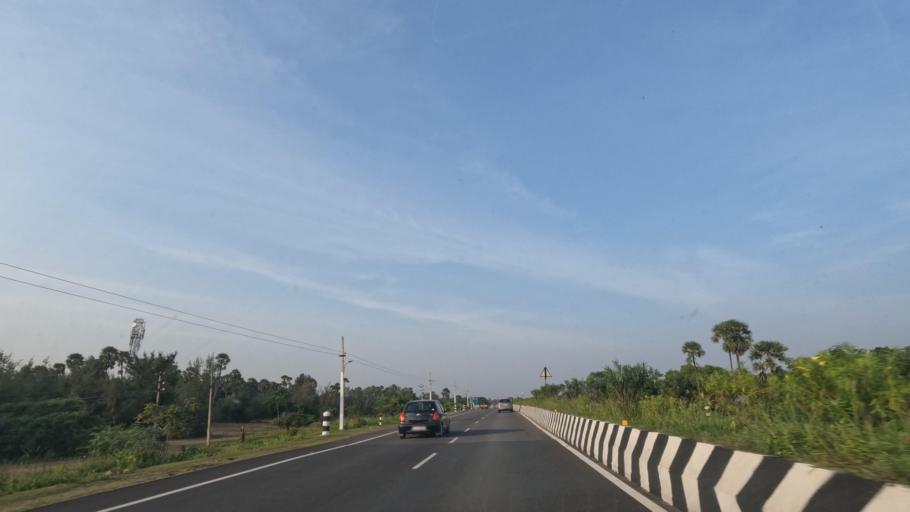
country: IN
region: Tamil Nadu
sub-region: Kancheepuram
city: Mamallapuram
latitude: 12.6796
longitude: 80.2136
